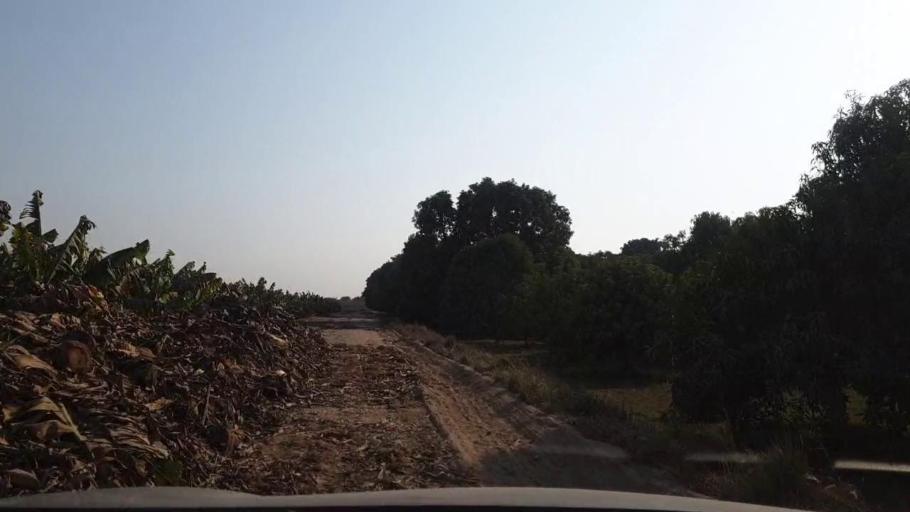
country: PK
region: Sindh
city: Tando Allahyar
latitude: 25.5709
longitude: 68.7642
